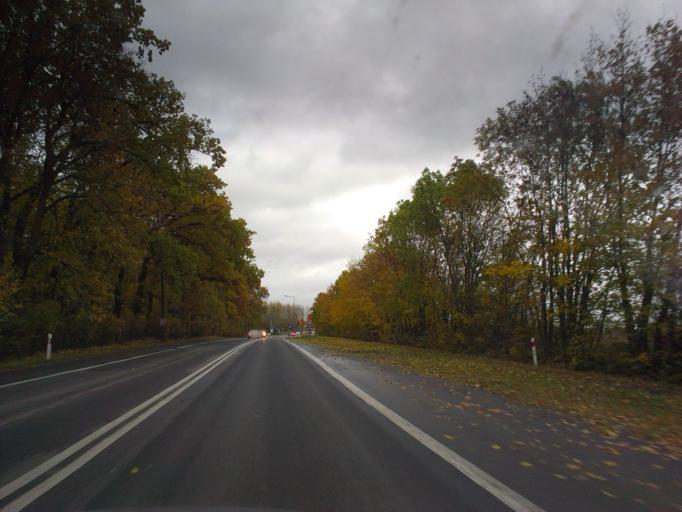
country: PL
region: Kujawsko-Pomorskie
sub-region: Powiat chelminski
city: Chelmno
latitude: 53.3384
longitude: 18.4654
